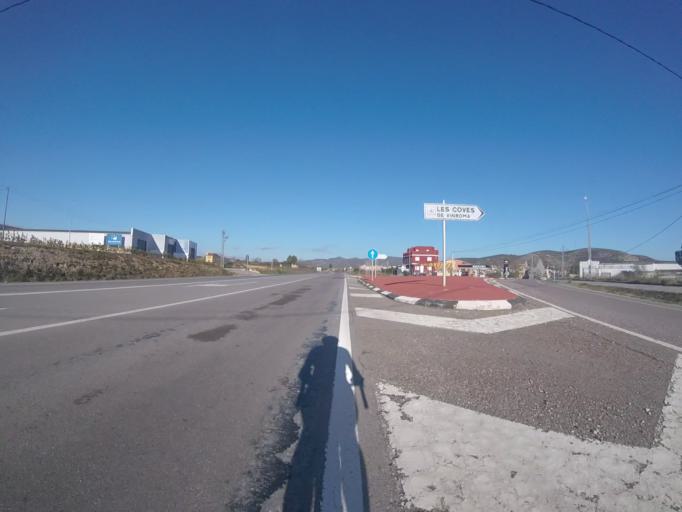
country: ES
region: Valencia
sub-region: Provincia de Castello
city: Cuevas de Vinroma
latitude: 40.3064
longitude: 0.1130
